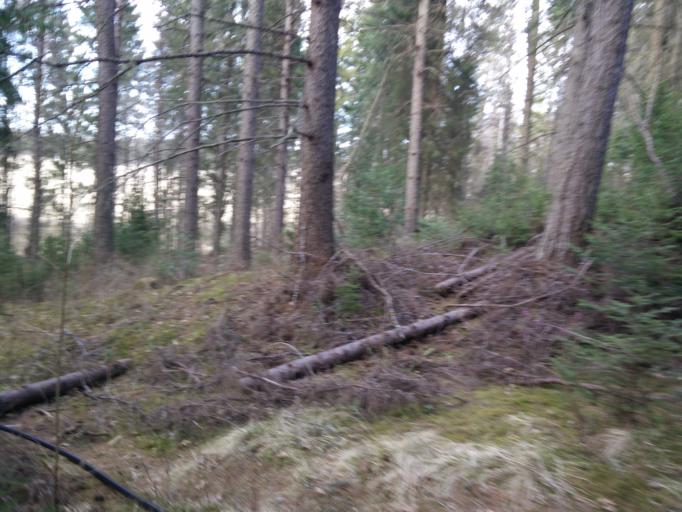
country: FI
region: Pirkanmaa
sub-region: Tampere
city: Orivesi
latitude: 61.7122
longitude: 24.3205
